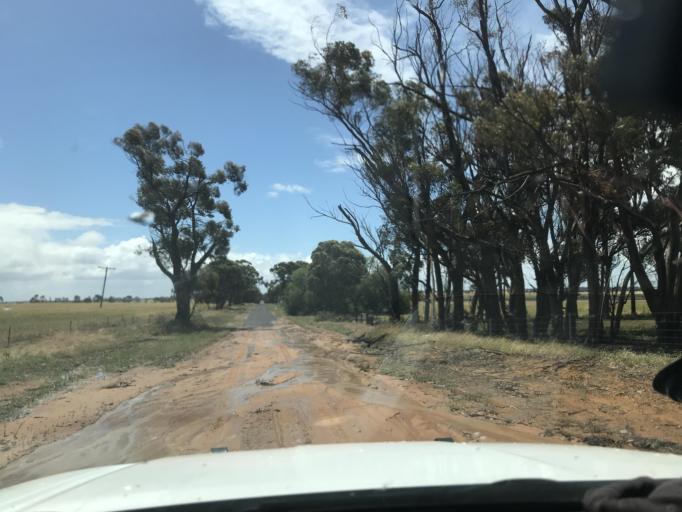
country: AU
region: South Australia
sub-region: Tatiara
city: Bordertown
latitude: -36.4469
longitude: 141.3246
